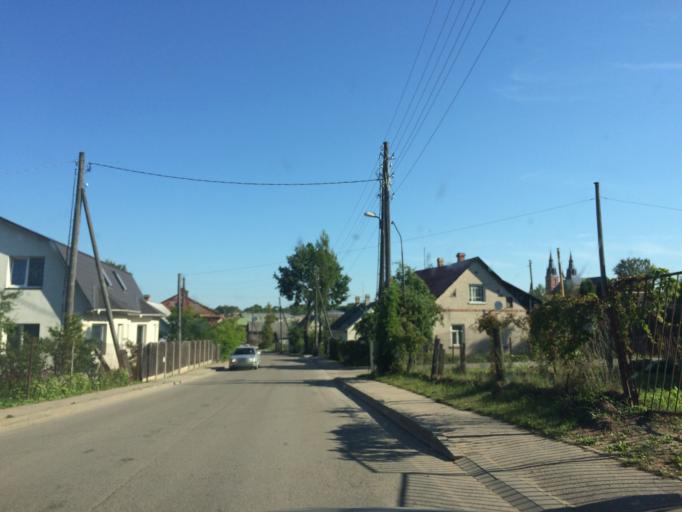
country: LV
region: Rezekne
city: Rezekne
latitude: 56.4960
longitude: 27.3354
